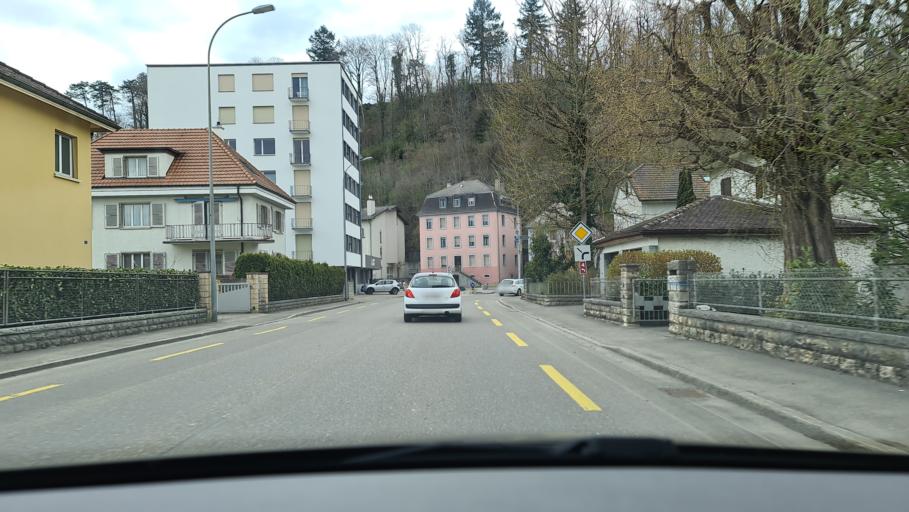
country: CH
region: Jura
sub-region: Porrentruy District
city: Porrentruy
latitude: 47.4215
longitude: 7.0779
